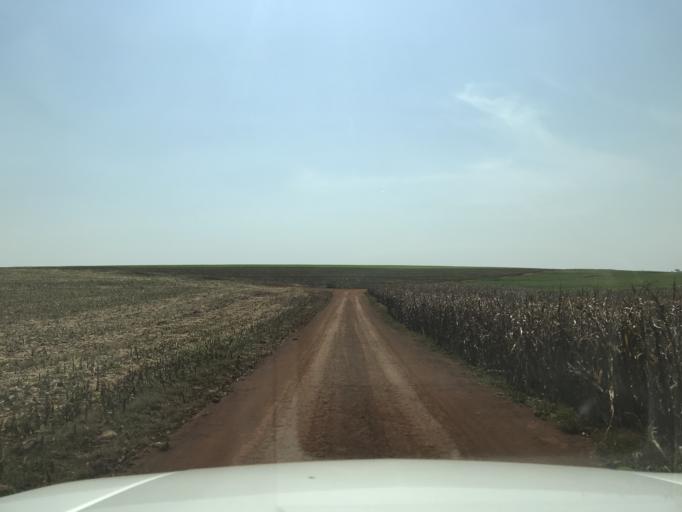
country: BR
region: Parana
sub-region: Palotina
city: Palotina
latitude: -24.2311
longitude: -53.7450
